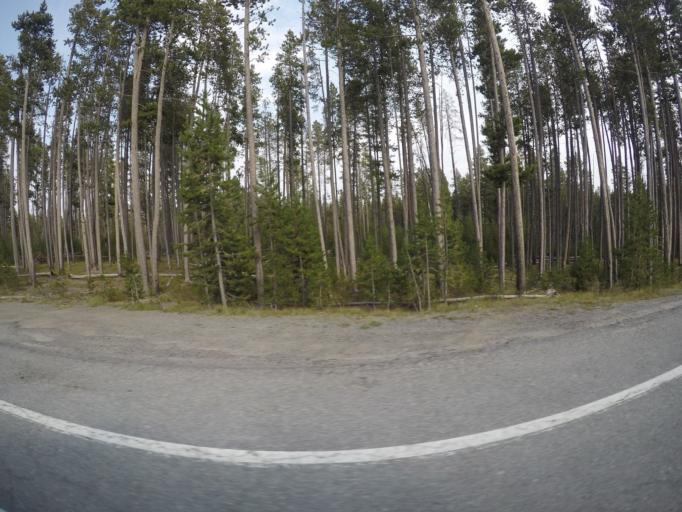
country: US
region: Montana
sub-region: Gallatin County
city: West Yellowstone
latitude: 44.7291
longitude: -110.6962
